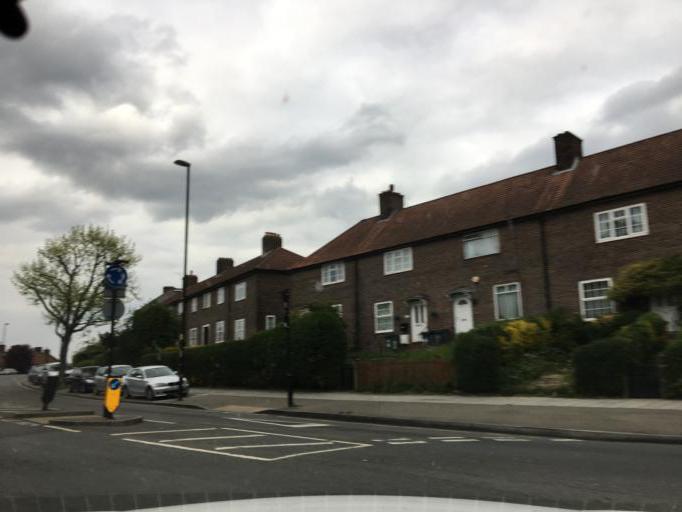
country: GB
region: England
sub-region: Greater London
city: Bromley
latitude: 51.4285
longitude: 0.0134
